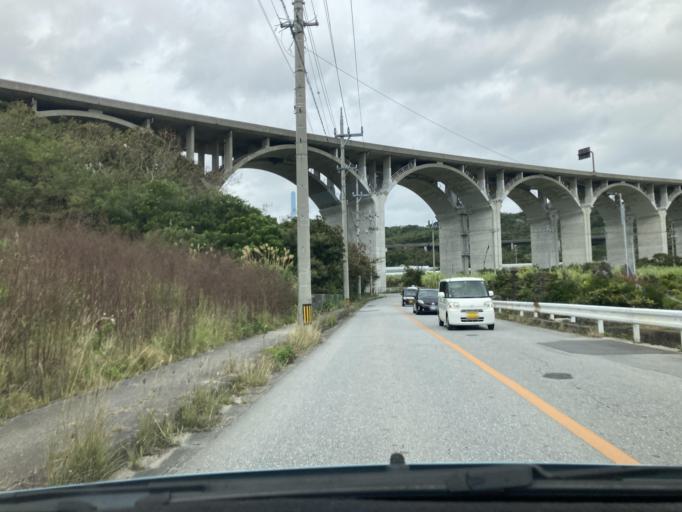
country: JP
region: Okinawa
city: Naha-shi
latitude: 26.2099
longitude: 127.7382
